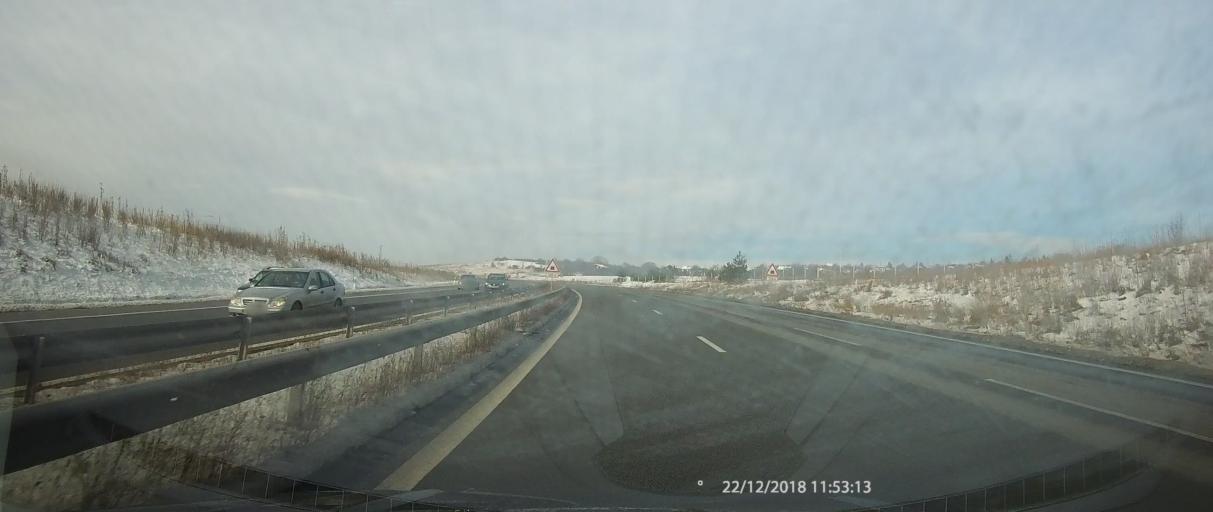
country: BG
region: Pernik
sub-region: Obshtina Pernik
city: Pernik
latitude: 42.6230
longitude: 23.1368
